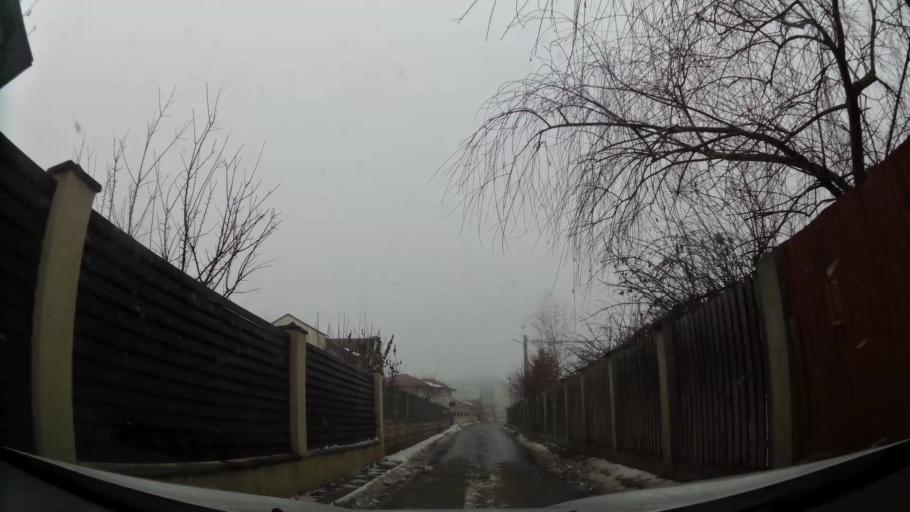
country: RO
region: Ilfov
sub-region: Comuna Chiajna
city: Chiajna
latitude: 44.4508
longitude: 25.9903
